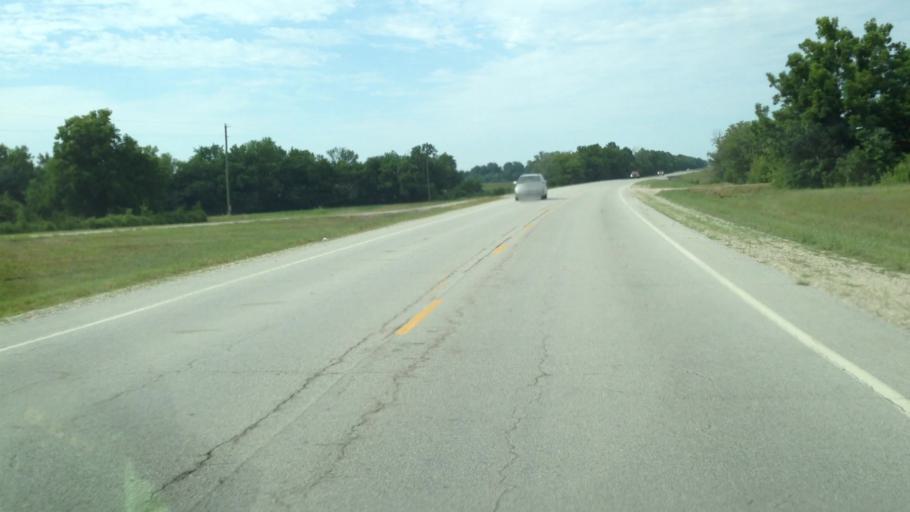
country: US
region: Kansas
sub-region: Labette County
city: Chetopa
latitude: 37.0546
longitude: -95.1024
